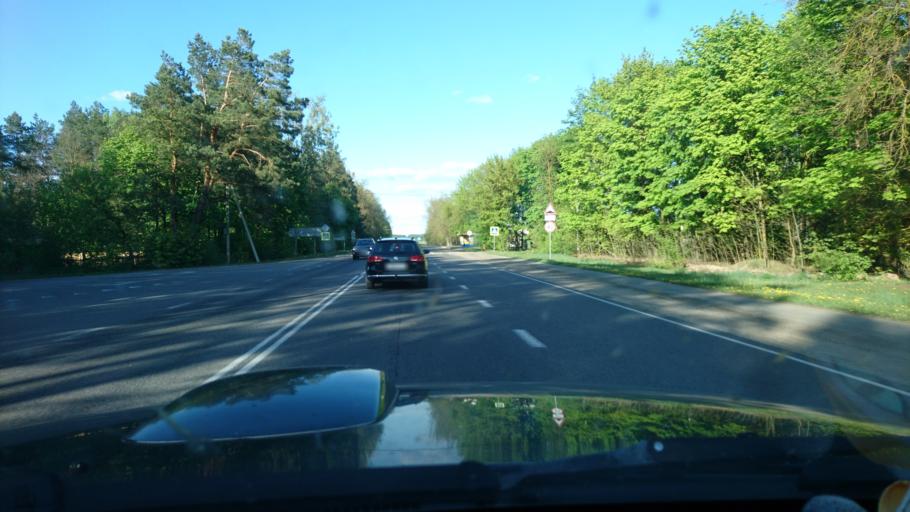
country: BY
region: Brest
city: Byaroza
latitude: 52.5471
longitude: 25.0102
